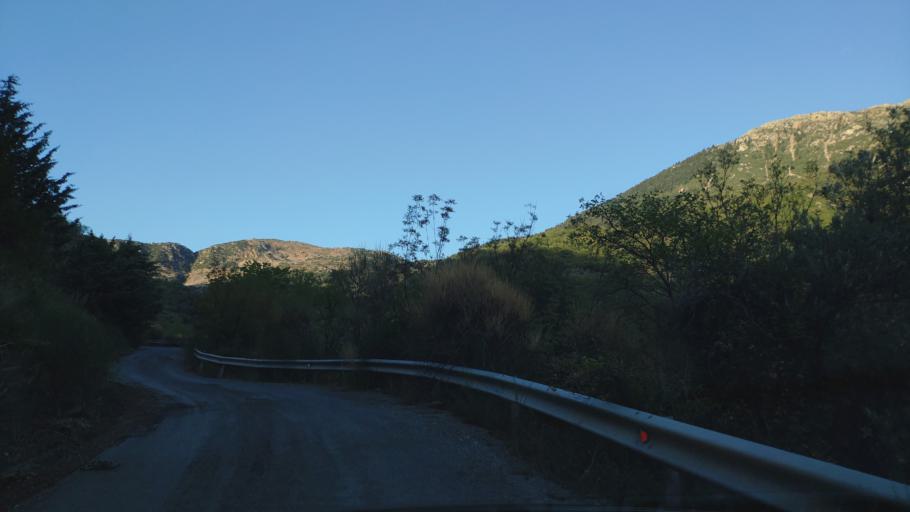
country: GR
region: Peloponnese
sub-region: Nomos Arkadias
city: Dimitsana
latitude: 37.5626
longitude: 22.0458
